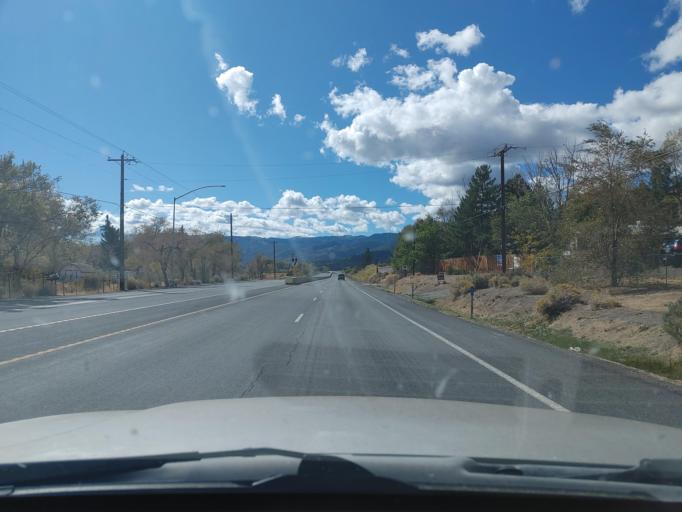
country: US
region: Nevada
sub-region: Carson City
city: Carson City
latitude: 39.3208
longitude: -119.8171
